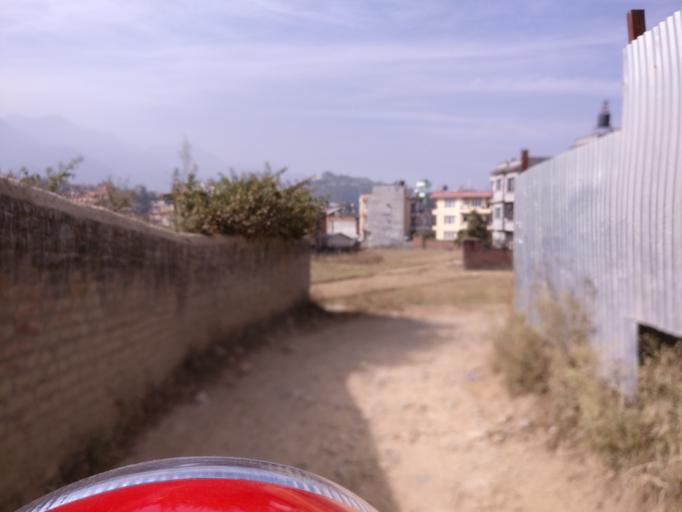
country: NP
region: Central Region
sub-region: Bagmati Zone
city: Patan
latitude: 27.6592
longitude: 85.3110
